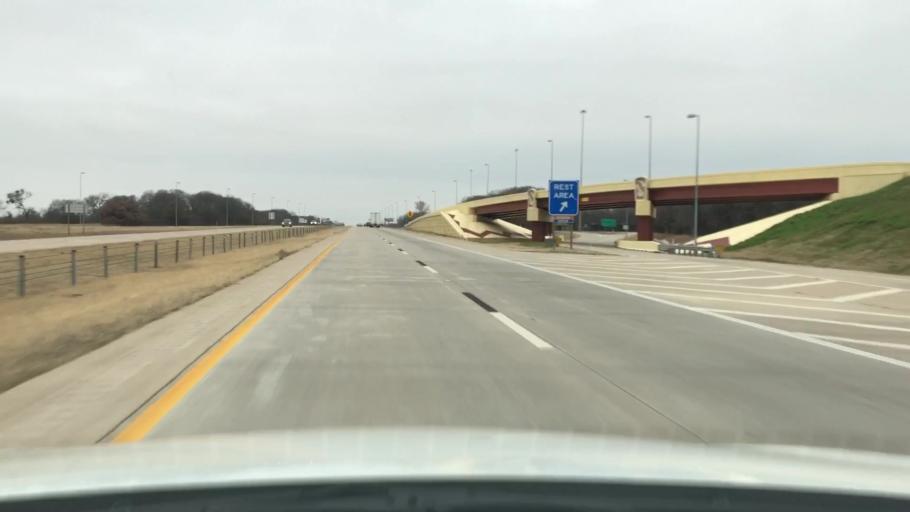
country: US
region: Texas
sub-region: Cooke County
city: Gainesville
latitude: 33.7680
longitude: -97.1348
